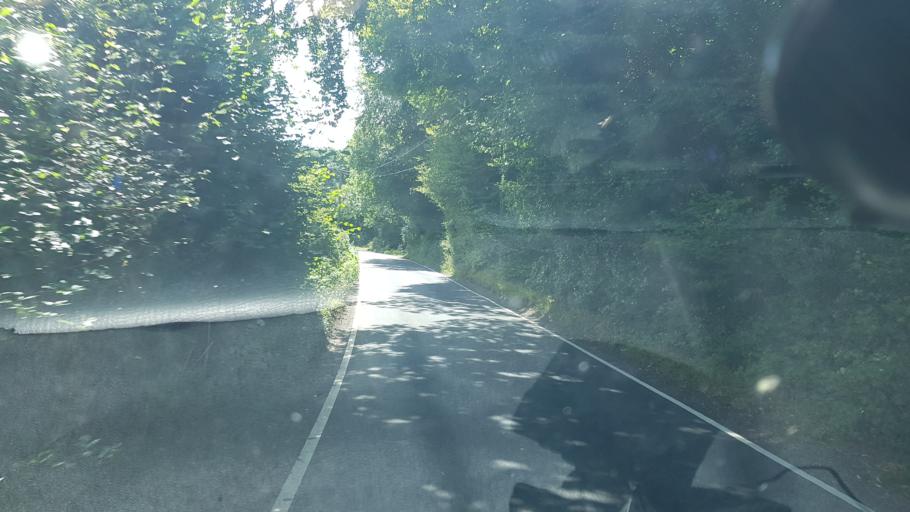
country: GB
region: England
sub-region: Kent
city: Edenbridge
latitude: 51.2239
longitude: 0.1291
